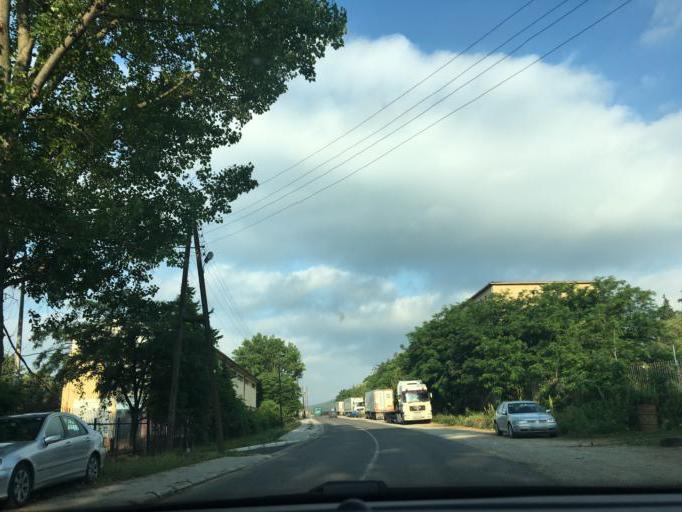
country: MK
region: Valandovo
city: Valandovo
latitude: 41.3197
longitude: 22.5702
